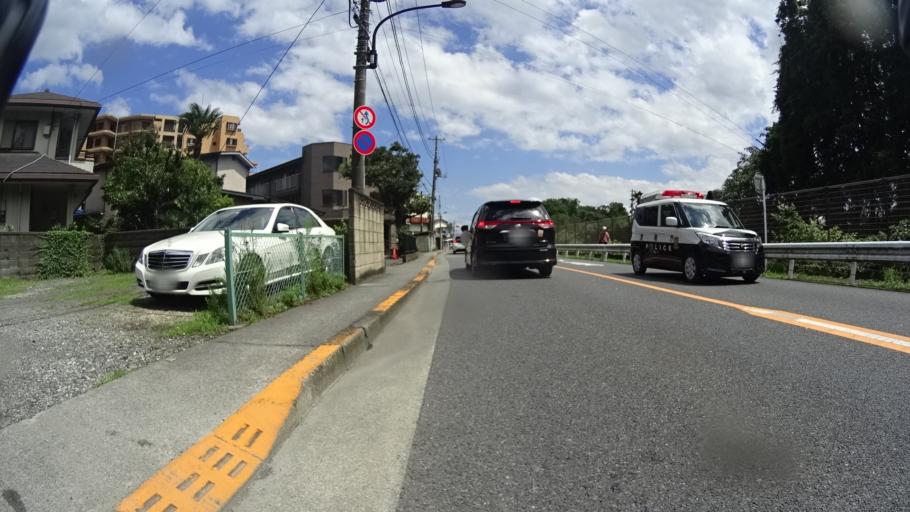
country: JP
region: Tokyo
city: Fussa
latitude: 35.7410
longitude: 139.3216
